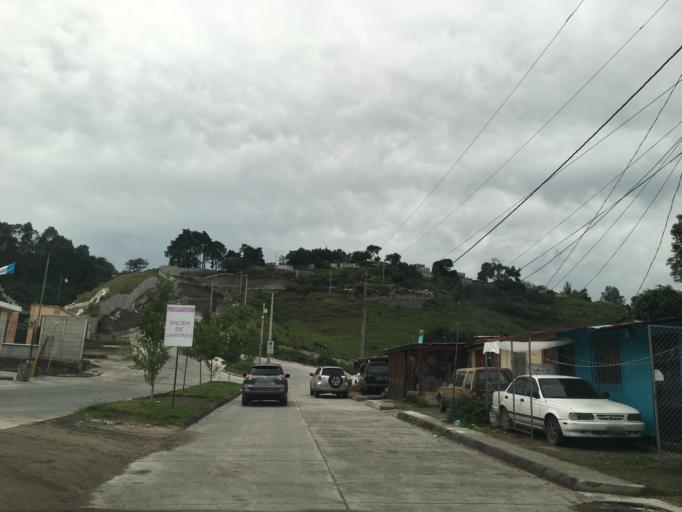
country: GT
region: Guatemala
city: Villa Nueva
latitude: 14.5187
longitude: -90.5672
